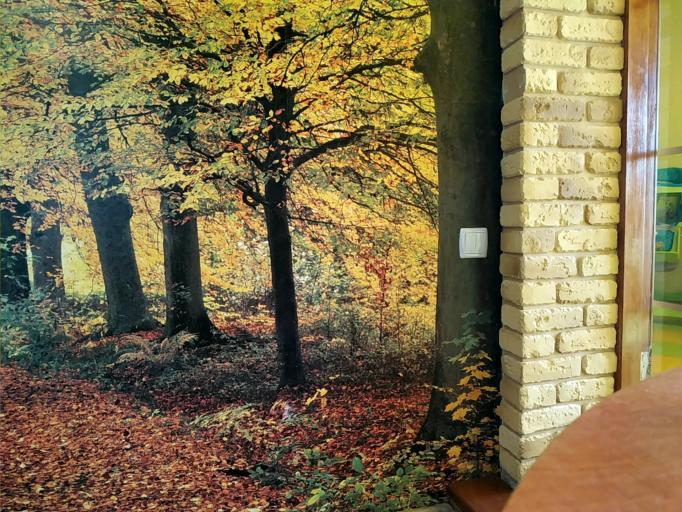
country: RU
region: Novgorod
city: Staraya Russa
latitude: 57.8314
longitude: 31.4894
